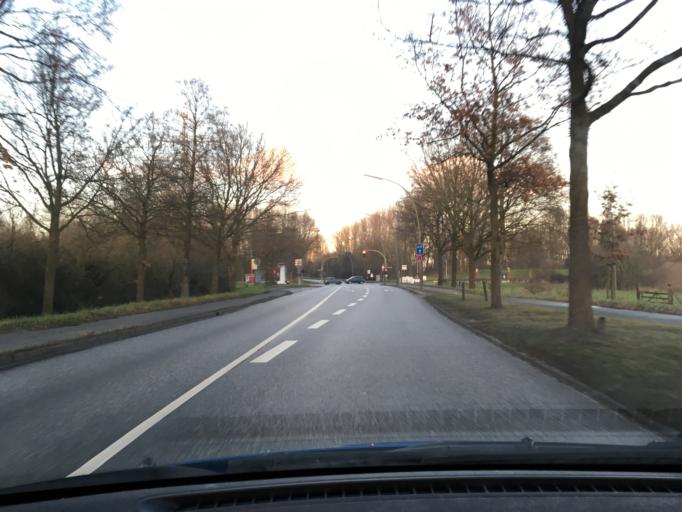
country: DE
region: Hamburg
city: Altona
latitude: 53.4944
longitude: 9.9096
